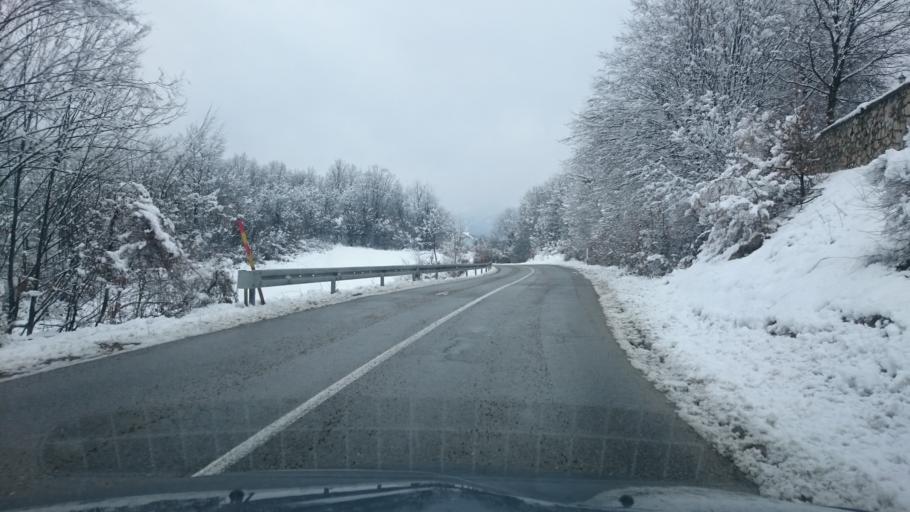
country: BA
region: Republika Srpska
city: Starcevica
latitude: 44.6411
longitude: 17.2366
